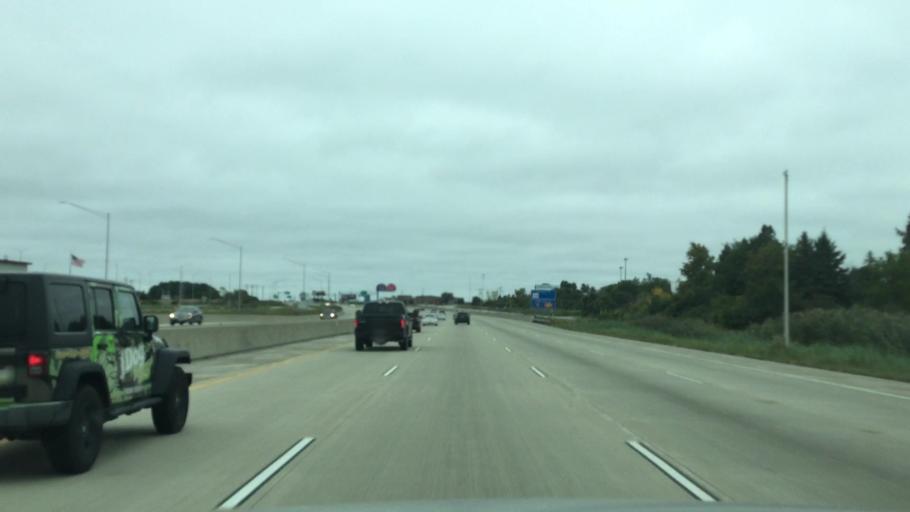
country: US
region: Wisconsin
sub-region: Kenosha County
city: Pleasant Prairie
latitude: 42.5015
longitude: -87.9515
